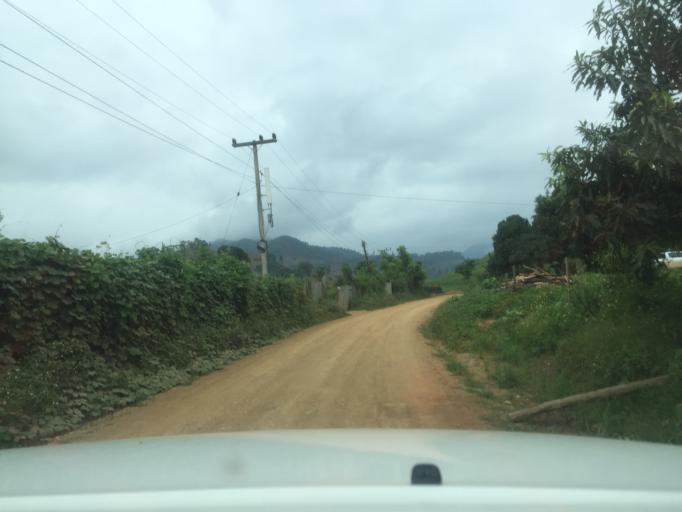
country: TH
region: Phayao
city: Phu Sang
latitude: 19.6958
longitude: 100.4974
